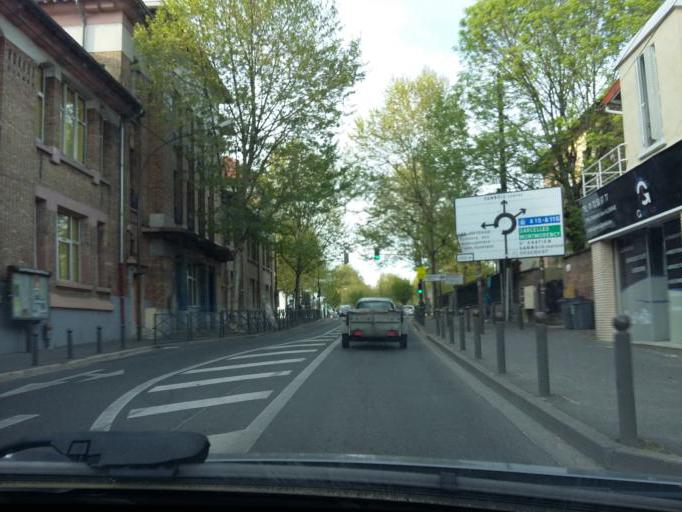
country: FR
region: Ile-de-France
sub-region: Departement du Val-d'Oise
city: Sannois
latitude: 48.9590
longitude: 2.2577
